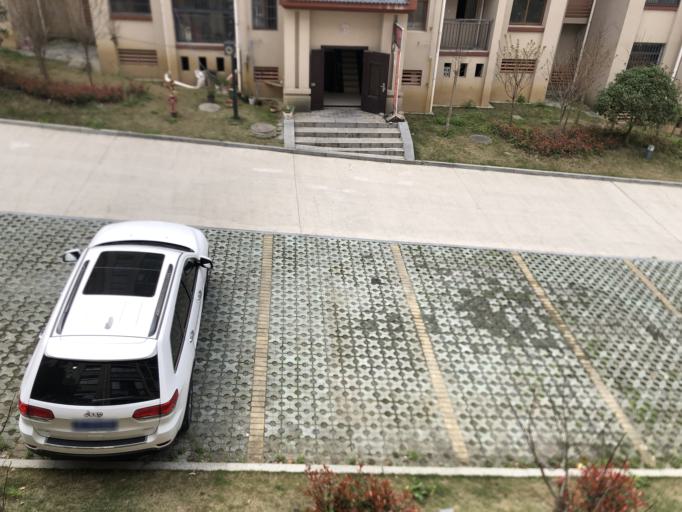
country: CN
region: Hubei
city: Yuyangguan
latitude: 30.1581
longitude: 111.0704
